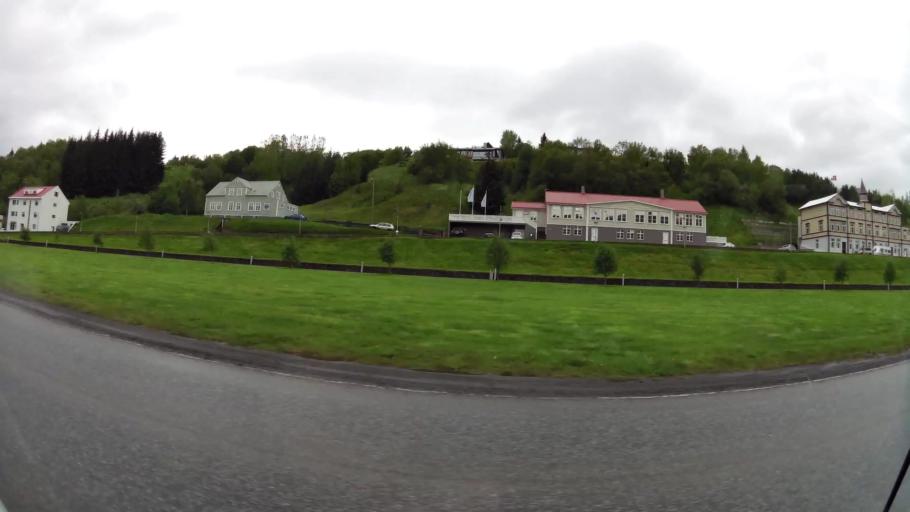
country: IS
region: Northeast
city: Akureyri
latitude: 65.6764
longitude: -18.0880
